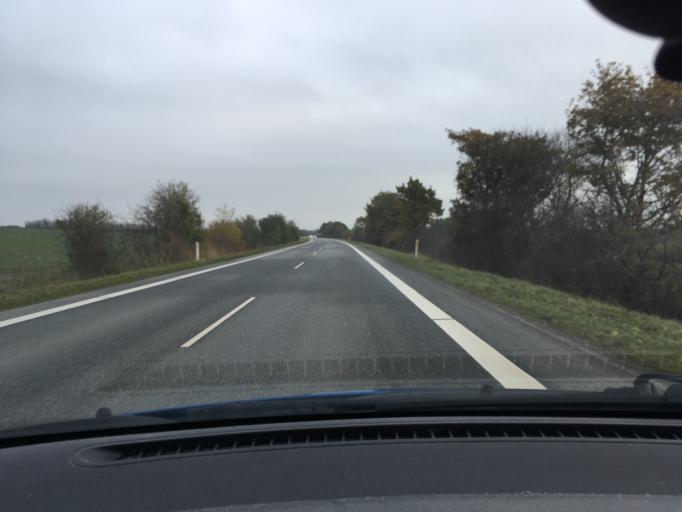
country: DK
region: South Denmark
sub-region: Aabenraa Kommune
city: Aabenraa
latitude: 54.9865
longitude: 9.3972
